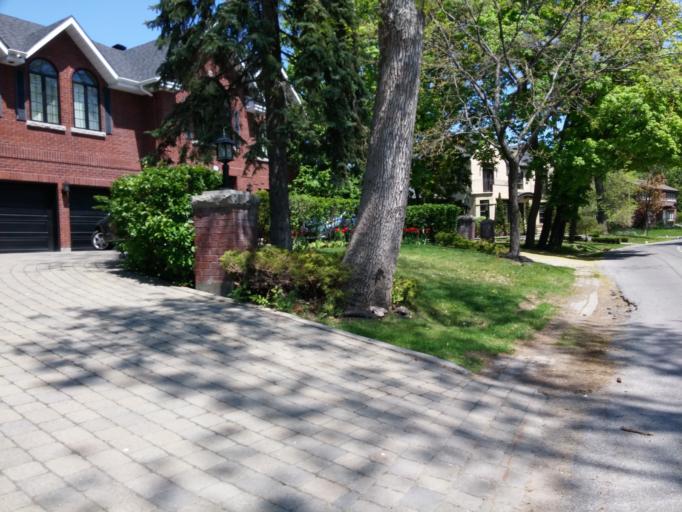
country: CA
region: Quebec
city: Beaconsfield
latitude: 45.4158
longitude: -73.8848
